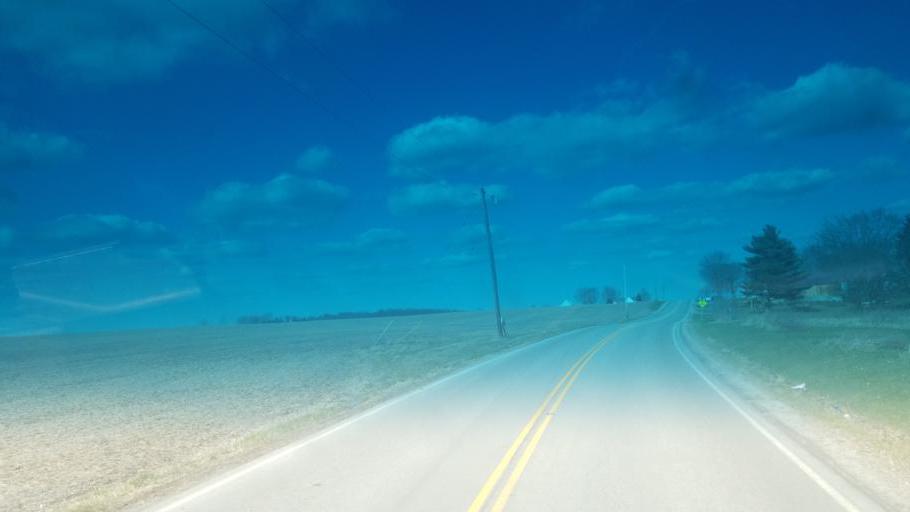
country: US
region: Ohio
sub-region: Highland County
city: Greenfield
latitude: 39.3023
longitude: -83.4425
